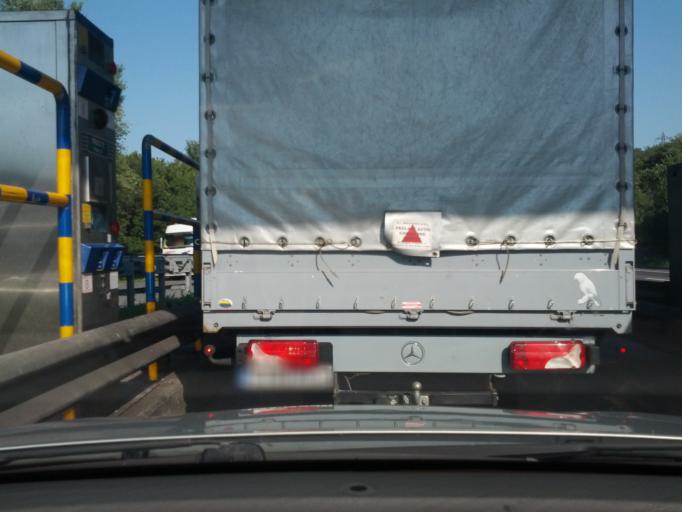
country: IT
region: Friuli Venezia Giulia
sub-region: Provincia di Gorizia
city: Monfalcone
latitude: 45.8055
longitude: 13.5773
